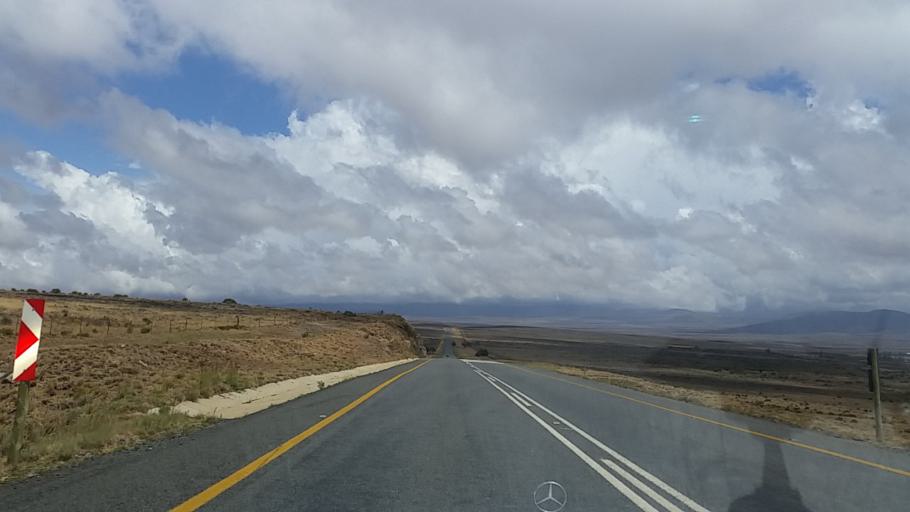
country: ZA
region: Eastern Cape
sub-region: Chris Hani District Municipality
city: Middelburg
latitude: -31.8562
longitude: 24.8678
